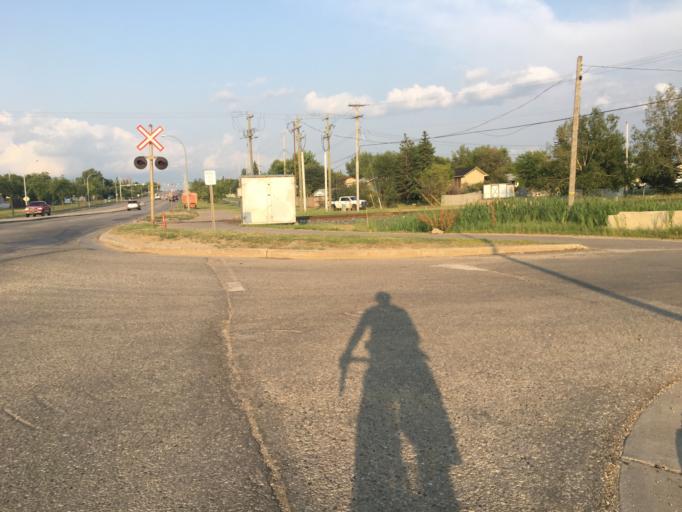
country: CA
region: Alberta
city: Grande Prairie
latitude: 55.1852
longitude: -118.7896
